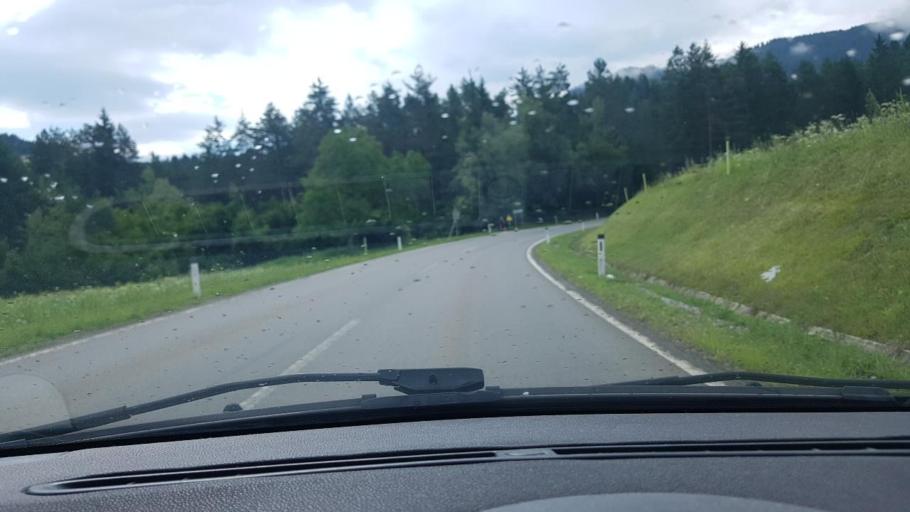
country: AT
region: Carinthia
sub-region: Politischer Bezirk Spittal an der Drau
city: Greifenburg
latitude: 46.7395
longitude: 13.2166
